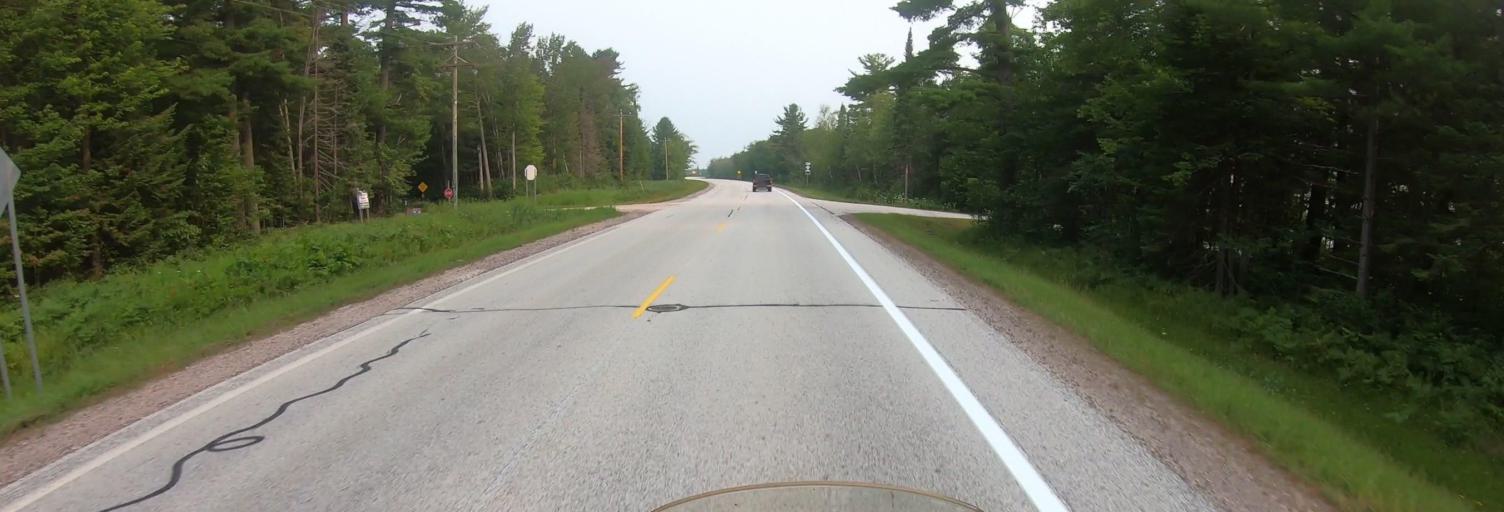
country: US
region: Michigan
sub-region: Luce County
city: Newberry
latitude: 46.5627
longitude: -85.0297
